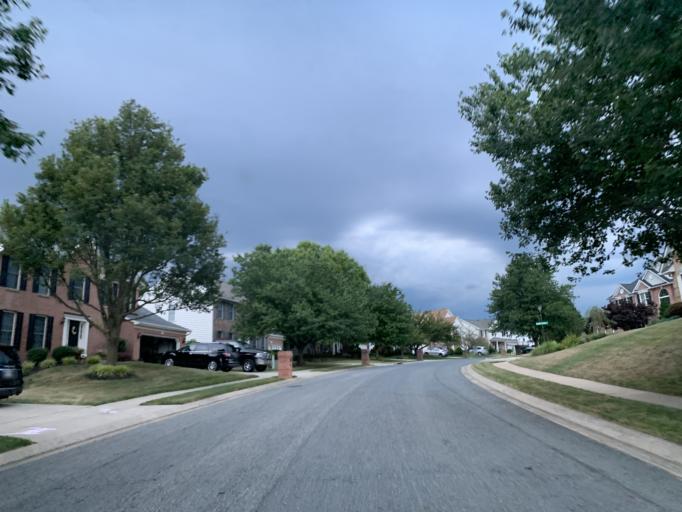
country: US
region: Maryland
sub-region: Harford County
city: Bel Air North
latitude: 39.5627
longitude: -76.3674
